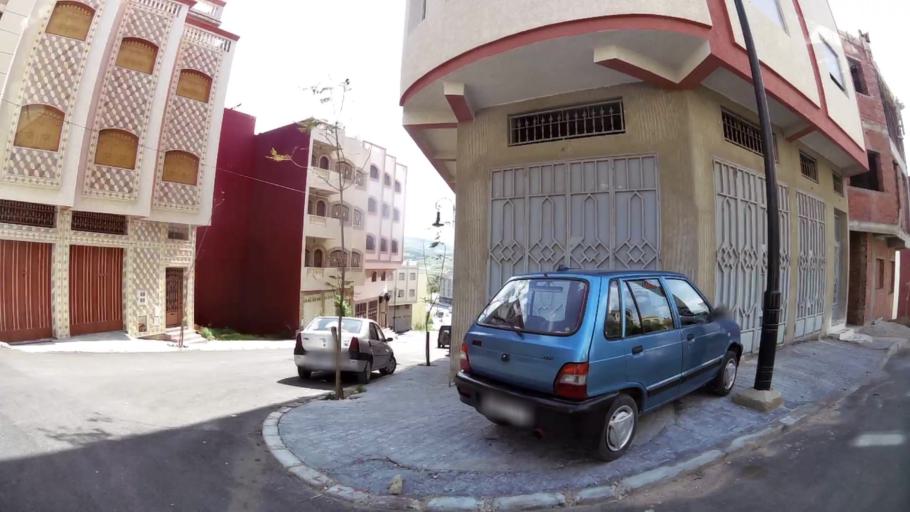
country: MA
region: Tanger-Tetouan
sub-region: Tanger-Assilah
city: Tangier
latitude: 35.7699
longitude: -5.7649
